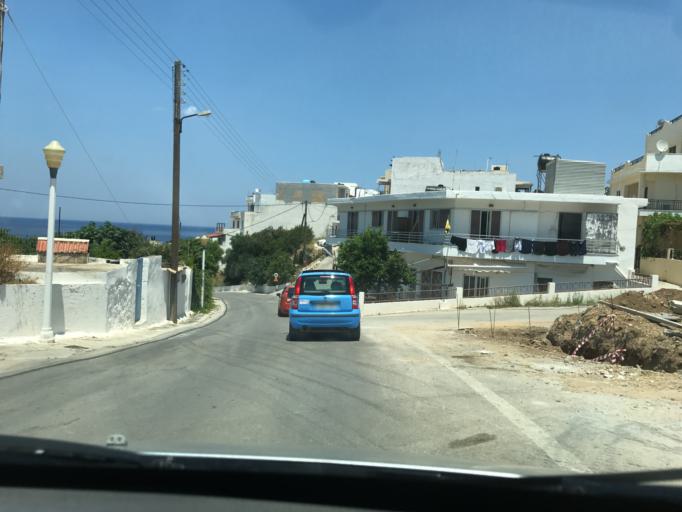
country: GR
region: South Aegean
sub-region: Nomos Dodekanisou
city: Karpathos
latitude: 35.5036
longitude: 27.2118
